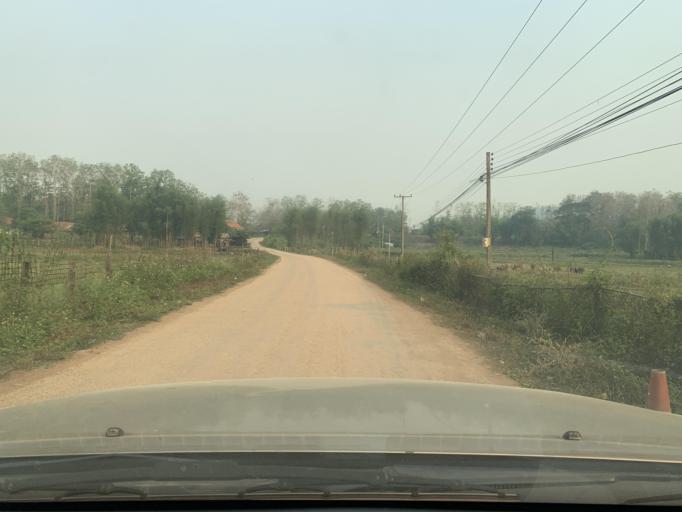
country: LA
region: Louangphabang
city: Louangphabang
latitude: 19.9154
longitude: 102.0748
